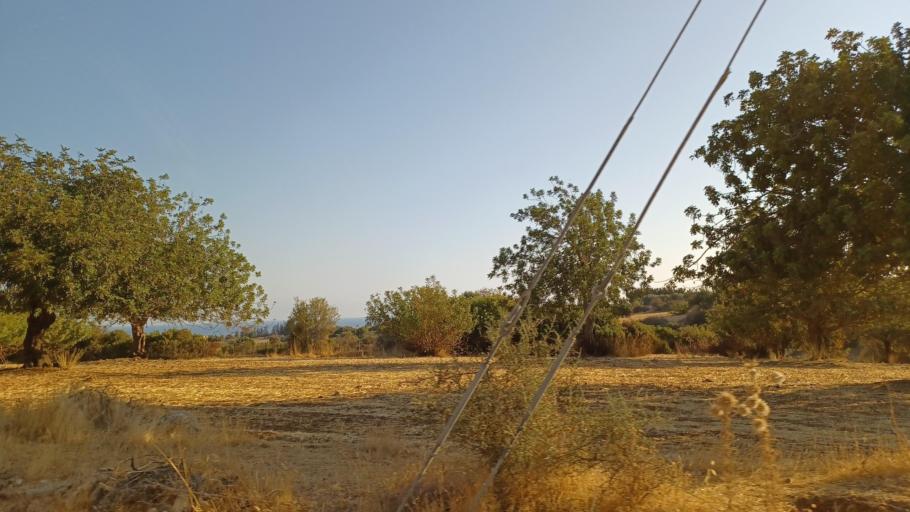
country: CY
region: Pafos
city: Polis
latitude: 35.0219
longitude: 32.3950
